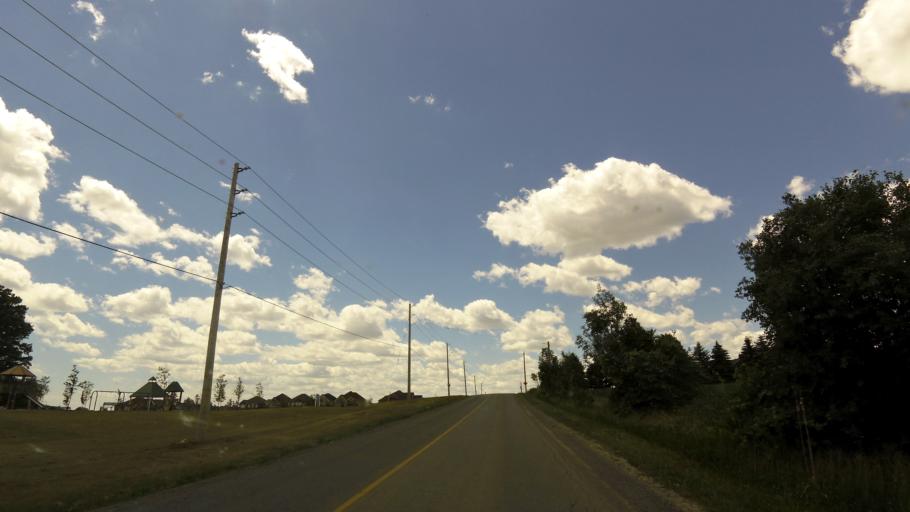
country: CA
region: Ontario
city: Oshawa
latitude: 43.9601
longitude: -78.8425
